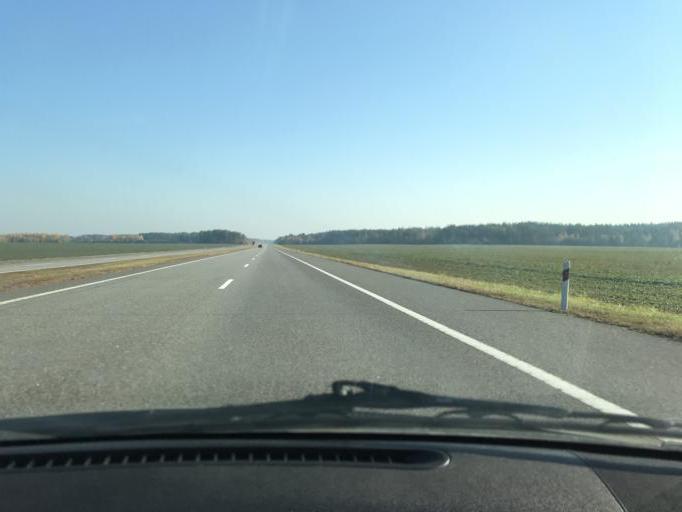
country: BY
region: Minsk
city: Bobr
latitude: 54.3864
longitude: 29.3750
